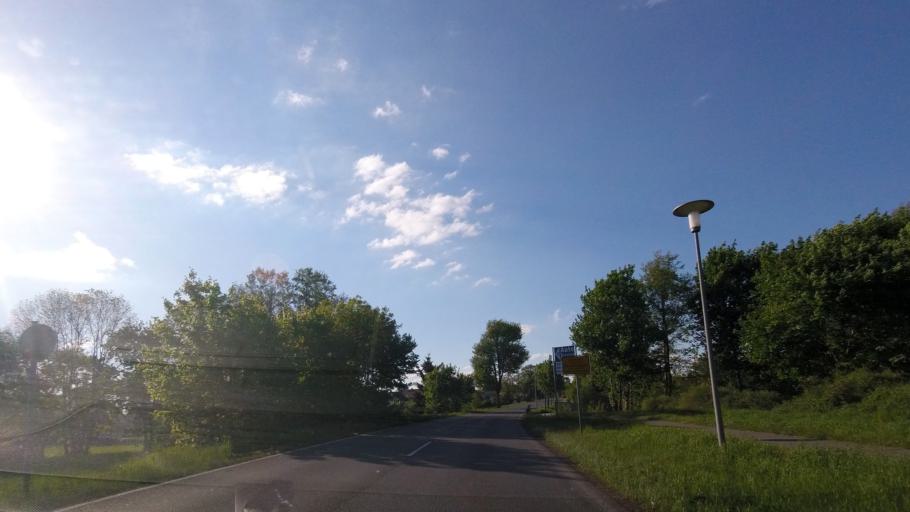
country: DE
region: Brandenburg
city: Lubbenau
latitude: 51.8669
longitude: 13.9199
